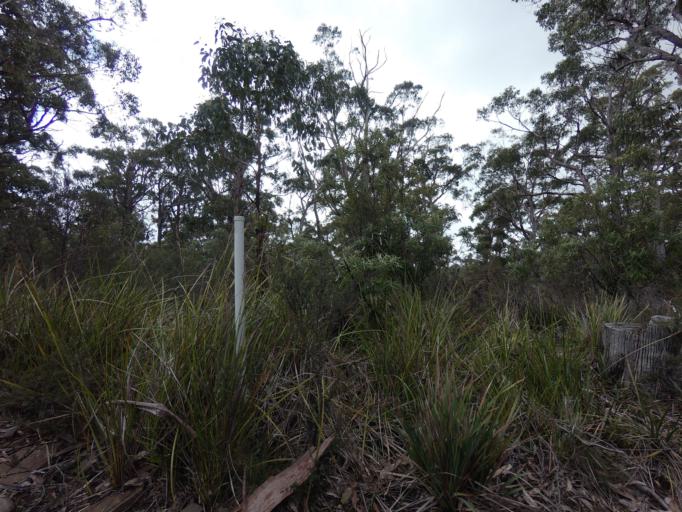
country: AU
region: Tasmania
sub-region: Huon Valley
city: Geeveston
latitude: -43.4646
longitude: 146.9187
